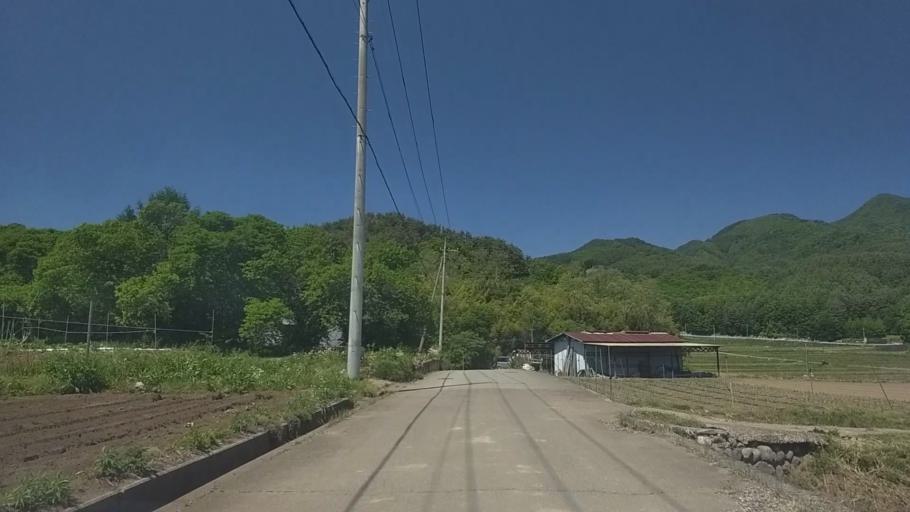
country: JP
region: Yamanashi
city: Nirasaki
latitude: 35.8542
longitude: 138.4418
